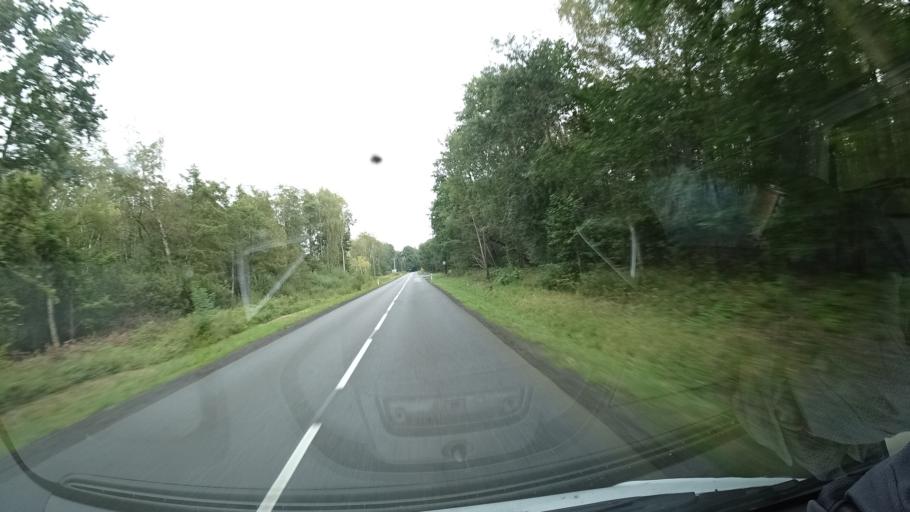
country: PL
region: Silesian Voivodeship
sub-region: Powiat gliwicki
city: Pyskowice
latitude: 50.3913
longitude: 18.5767
